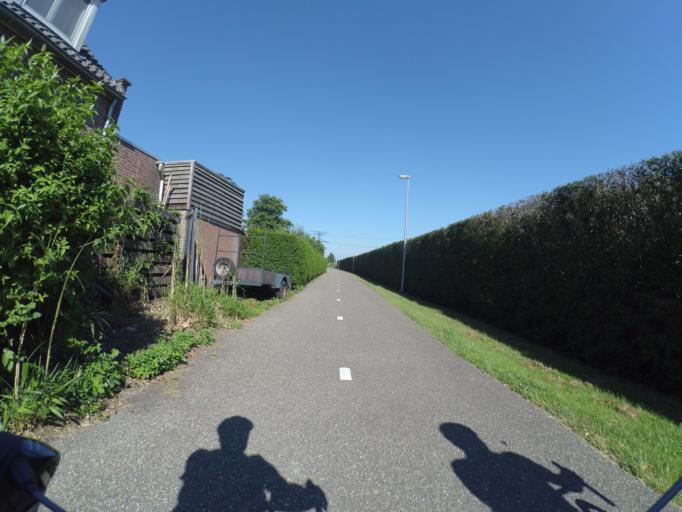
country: NL
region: North Brabant
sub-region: Gemeente Made en Drimmelen
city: Made
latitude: 51.6903
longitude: 4.7384
